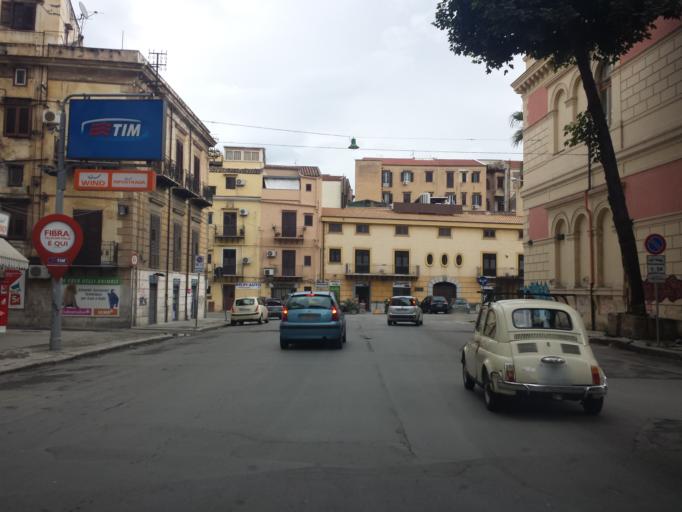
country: IT
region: Sicily
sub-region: Palermo
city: Palermo
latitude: 38.1201
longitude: 13.3524
